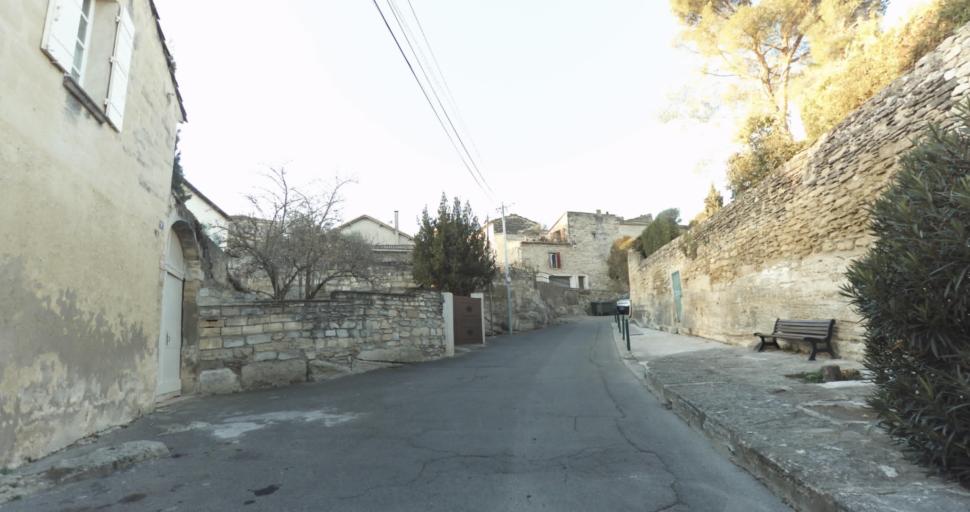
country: FR
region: Provence-Alpes-Cote d'Azur
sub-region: Departement des Bouches-du-Rhone
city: Barbentane
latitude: 43.9003
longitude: 4.7493
